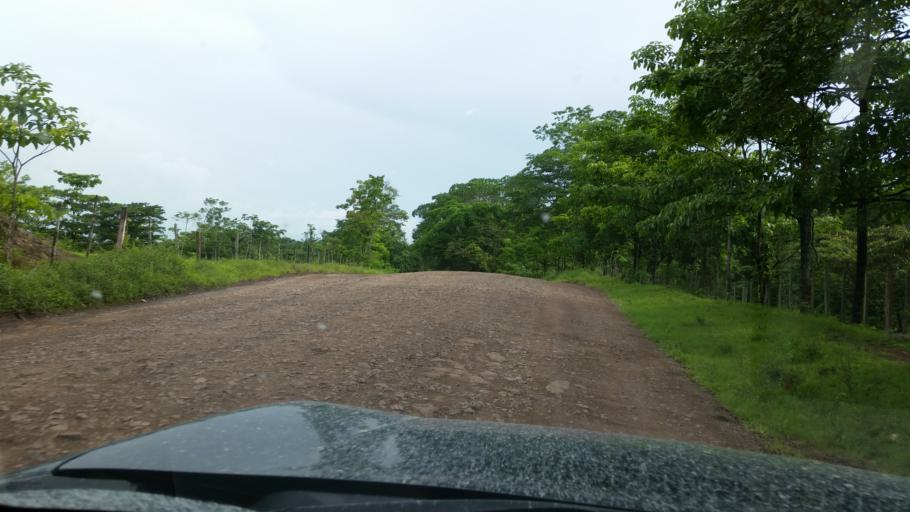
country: NI
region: Atlantico Norte (RAAN)
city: Siuna
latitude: 13.4535
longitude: -84.8530
